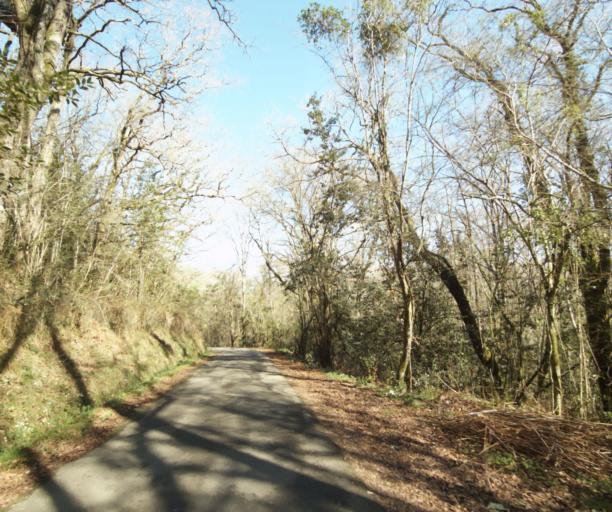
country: FR
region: Aquitaine
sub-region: Departement des Pyrenees-Atlantiques
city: Ciboure
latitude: 43.3665
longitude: -1.6724
